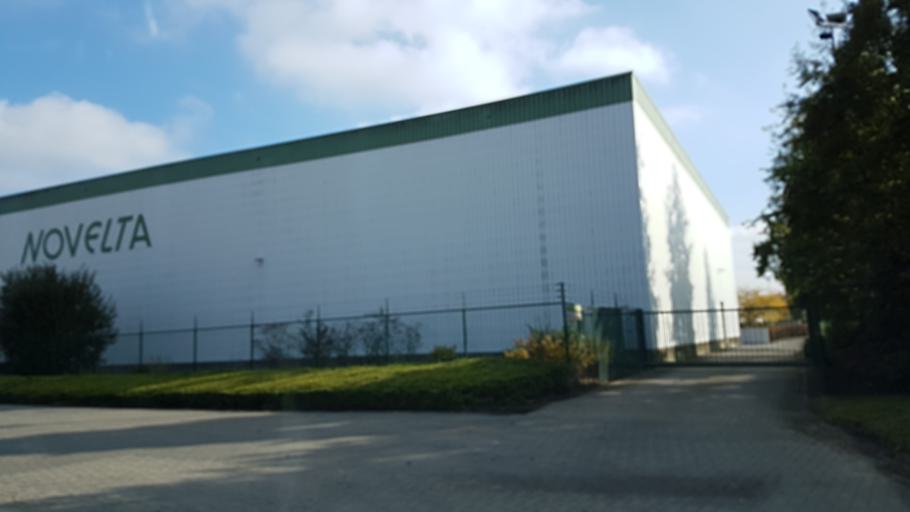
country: BE
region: Flanders
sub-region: Provincie Antwerpen
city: Kontich
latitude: 51.1259
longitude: 4.4207
